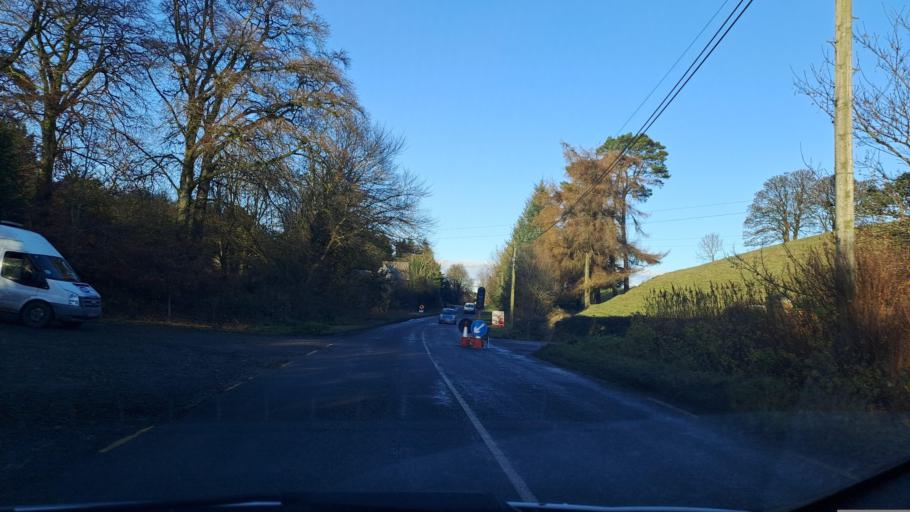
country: IE
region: Ulster
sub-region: An Cabhan
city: Bailieborough
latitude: 53.9003
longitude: -6.9667
